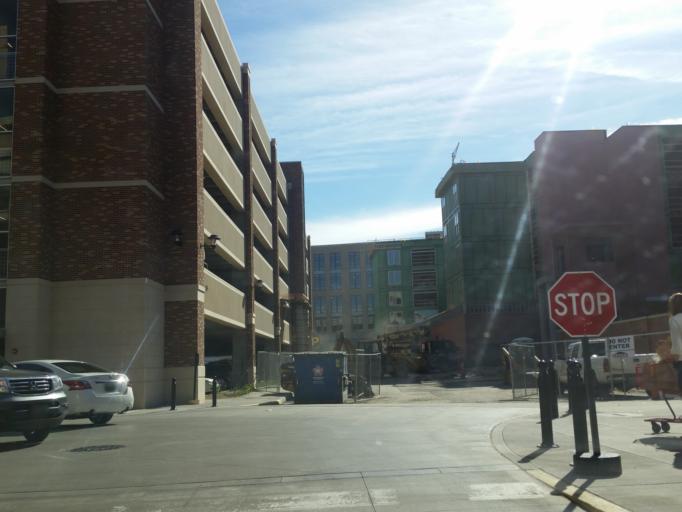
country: US
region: Ohio
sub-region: Cuyahoga County
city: Westlake
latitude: 41.4570
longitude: -81.9508
